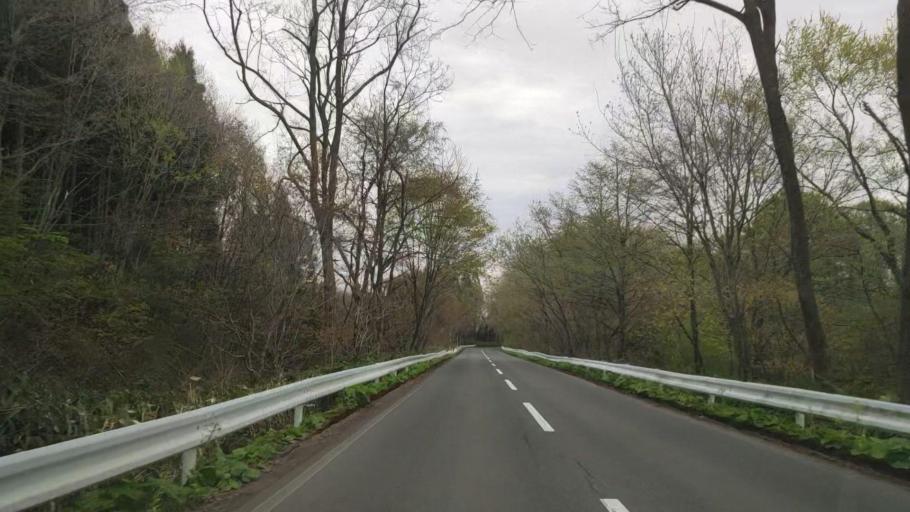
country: JP
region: Akita
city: Hanawa
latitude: 40.3810
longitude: 140.7908
